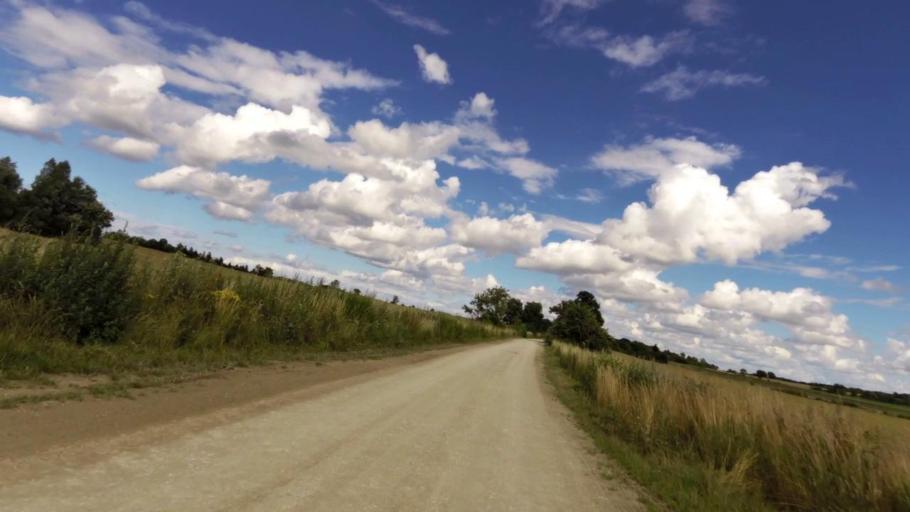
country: PL
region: Pomeranian Voivodeship
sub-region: Powiat slupski
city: Ustka
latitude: 54.5166
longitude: 16.7197
